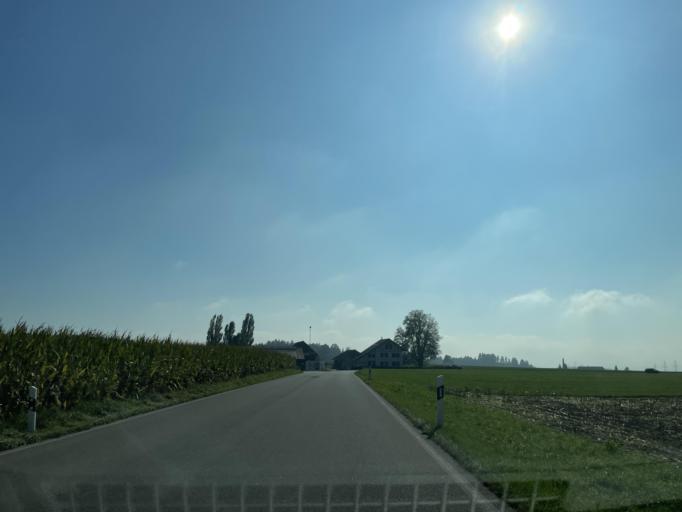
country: CH
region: Zurich
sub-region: Bezirk Winterthur
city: Brutten
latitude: 47.4658
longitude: 8.6677
